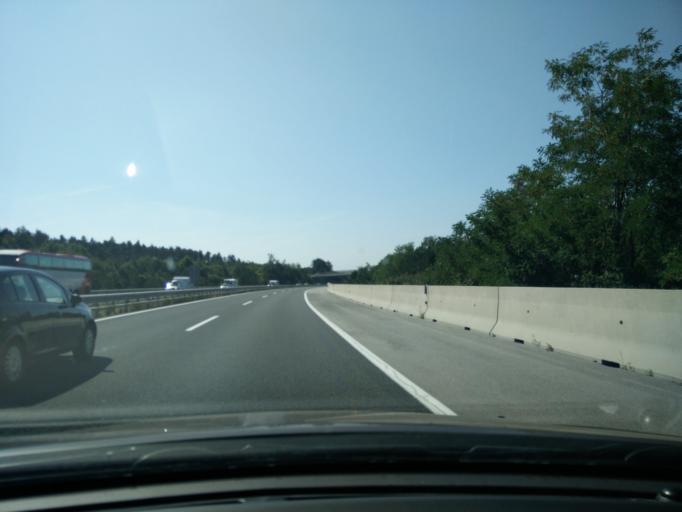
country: SI
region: Divaca
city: Divaca
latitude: 45.7090
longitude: 14.0016
